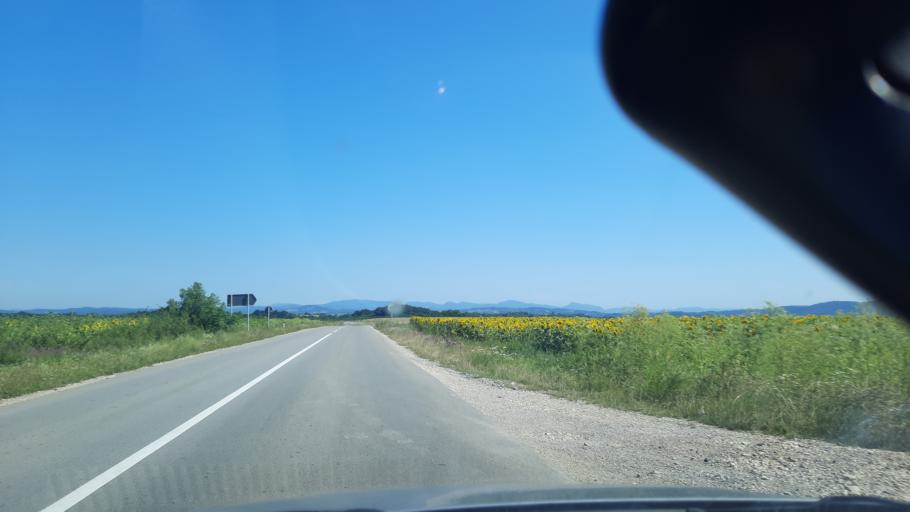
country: RS
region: Central Serbia
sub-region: Branicevski Okrug
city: Malo Crnice
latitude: 44.5634
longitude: 21.4339
